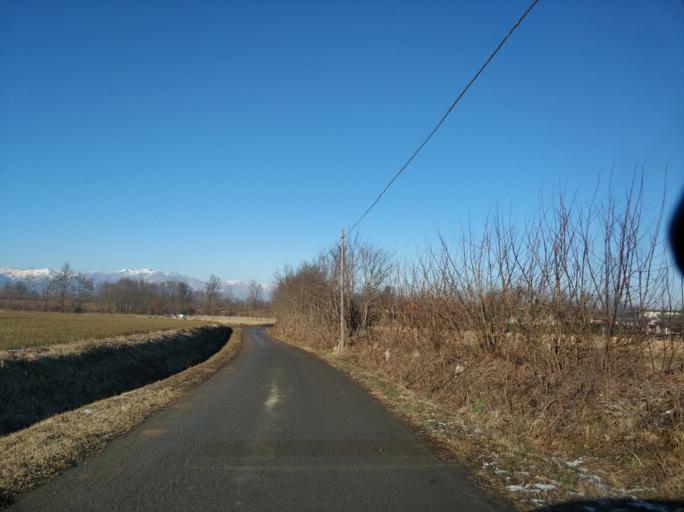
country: IT
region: Piedmont
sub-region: Provincia di Torino
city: San Francesco al Campo
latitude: 45.2211
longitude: 7.6794
